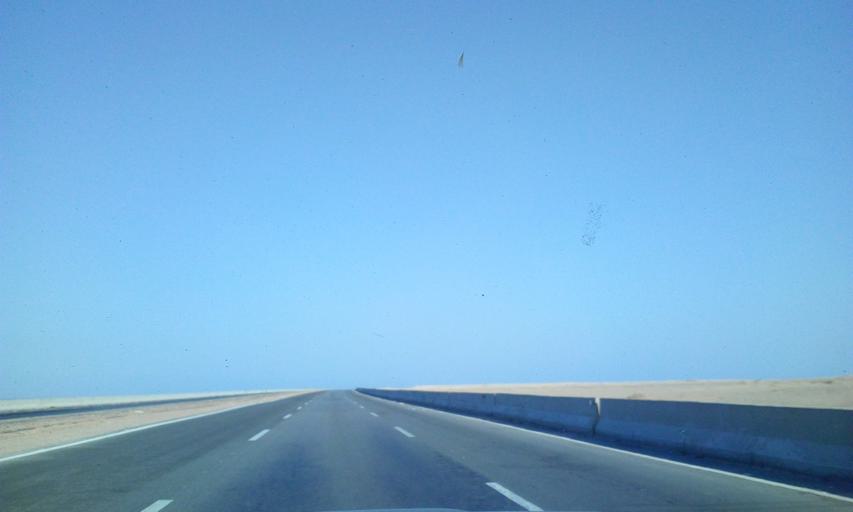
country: EG
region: As Suways
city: Ain Sukhna
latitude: 29.1048
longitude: 32.6109
